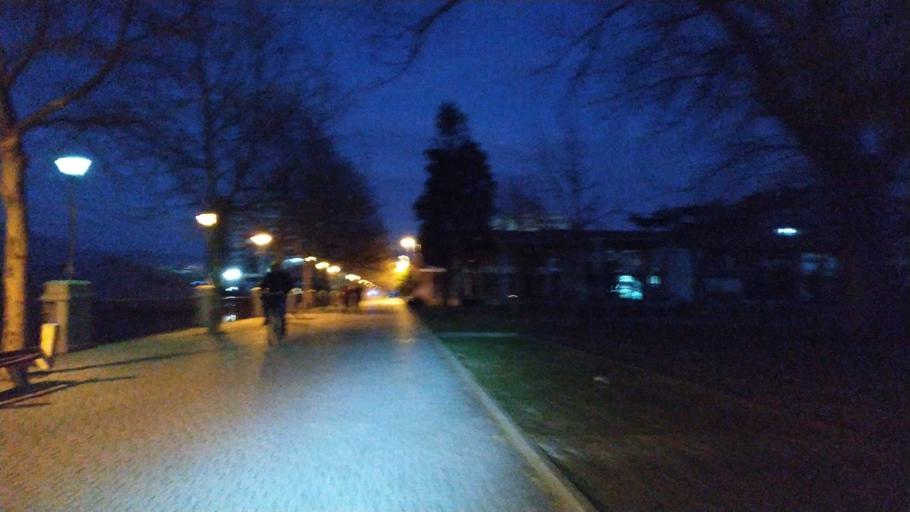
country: AL
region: Shkoder
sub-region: Rrethi i Shkodres
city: Shkoder
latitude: 42.0528
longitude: 19.4950
